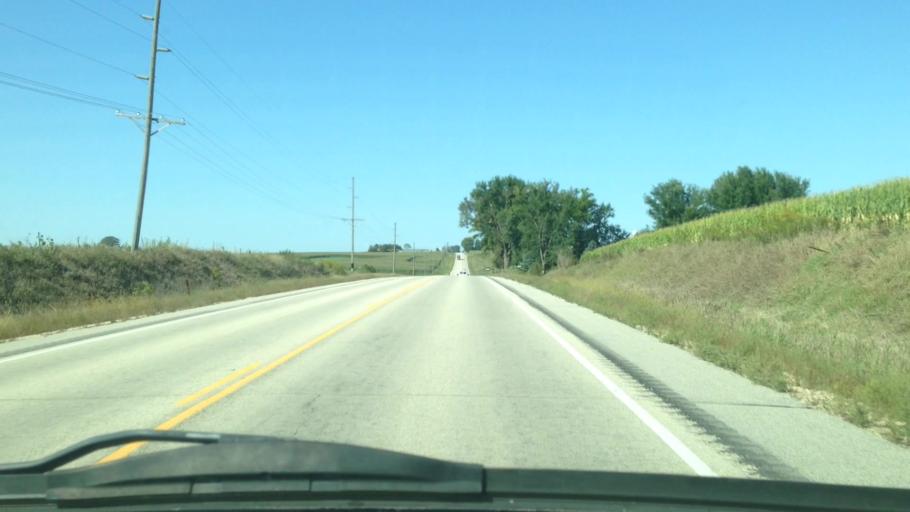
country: US
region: Minnesota
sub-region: Fillmore County
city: Rushford
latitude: 43.9067
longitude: -91.7401
